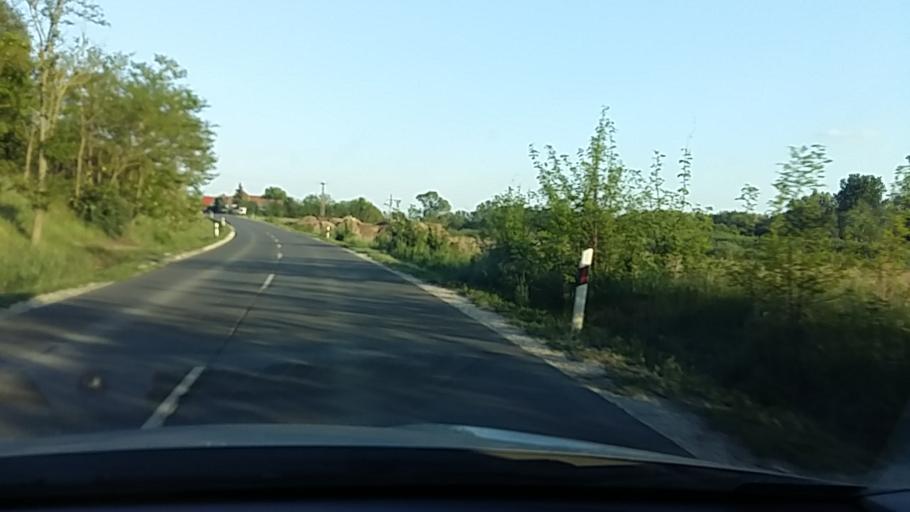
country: HU
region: Pest
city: Orbottyan
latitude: 47.6679
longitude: 19.2734
